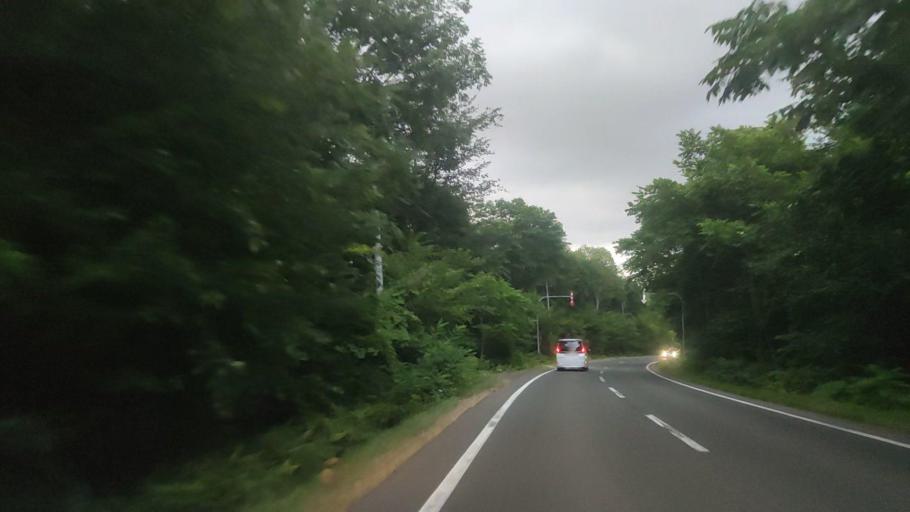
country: JP
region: Hokkaido
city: Shimo-furano
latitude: 43.3701
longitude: 142.3304
